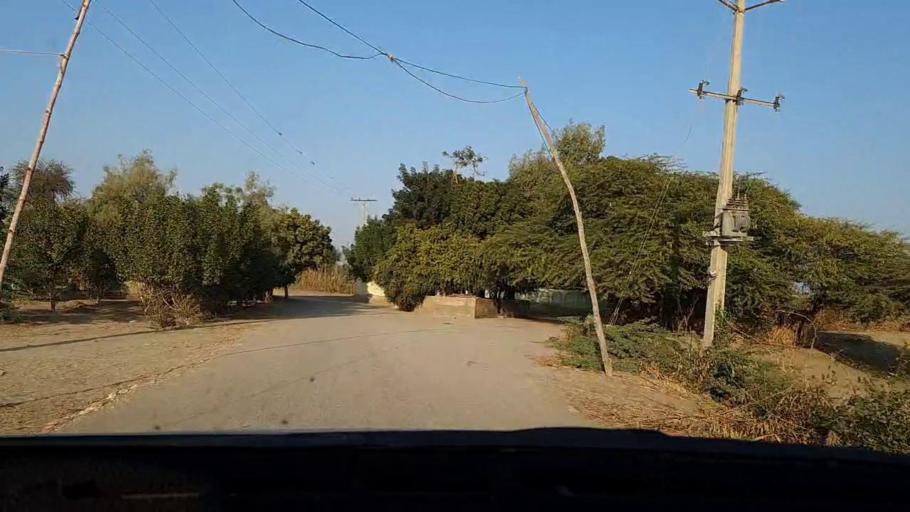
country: PK
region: Sindh
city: Tando Mittha Khan
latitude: 25.8733
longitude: 69.3125
